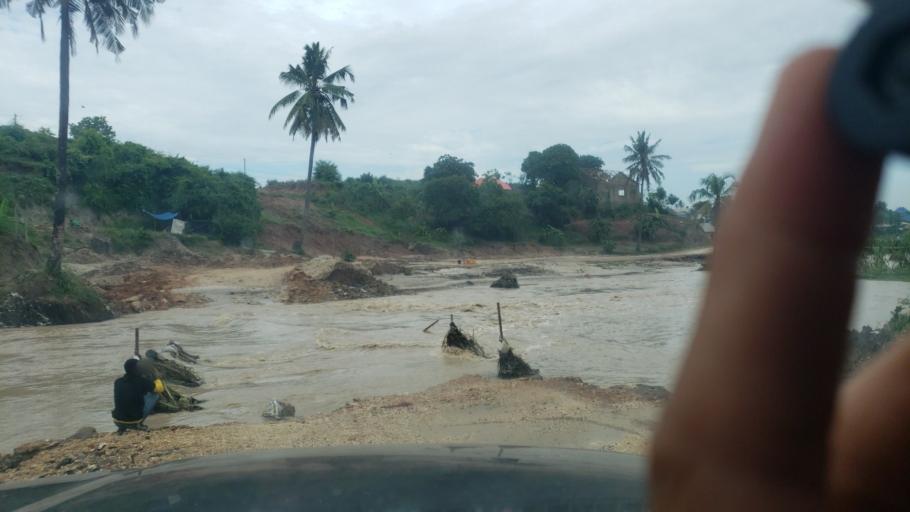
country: TZ
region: Dar es Salaam
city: Dar es Salaam
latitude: -6.9068
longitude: 39.2383
